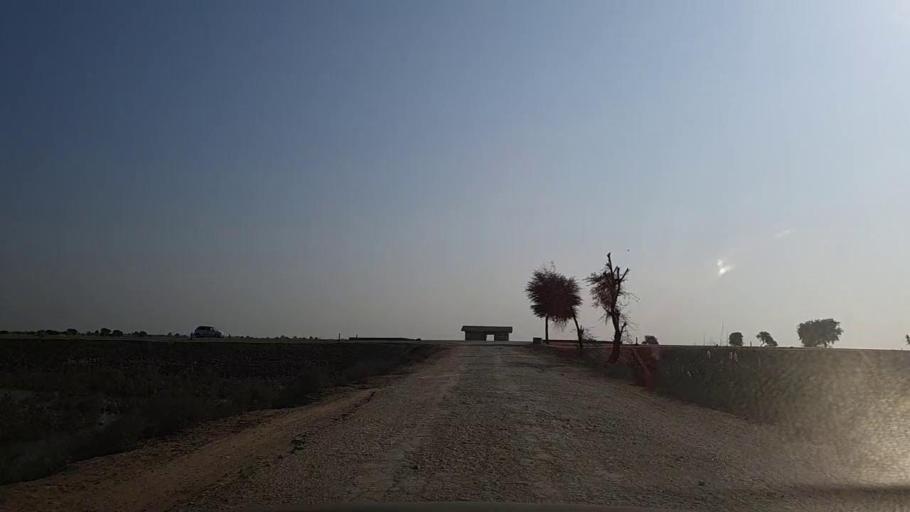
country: PK
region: Sindh
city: Tando Mittha Khan
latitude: 25.8825
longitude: 69.0767
